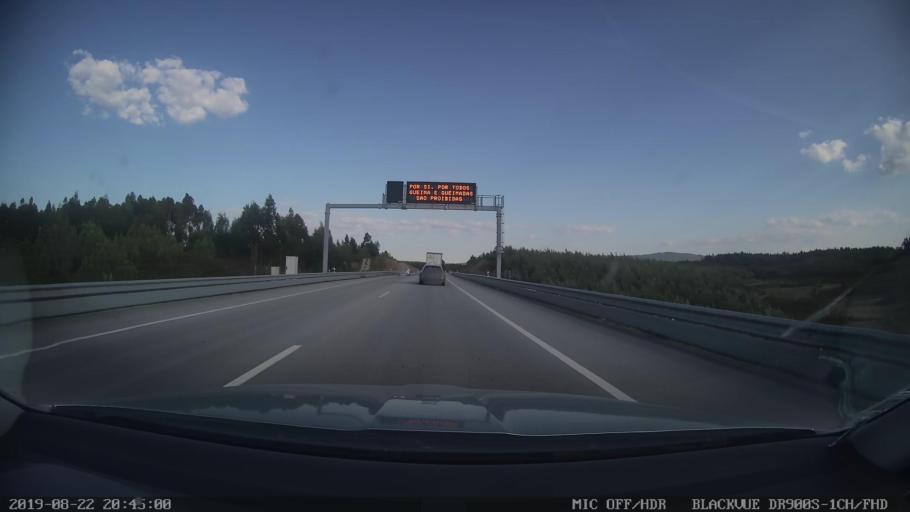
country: PT
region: Castelo Branco
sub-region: Proenca-A-Nova
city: Proenca-a-Nova
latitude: 39.7125
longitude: -7.8609
